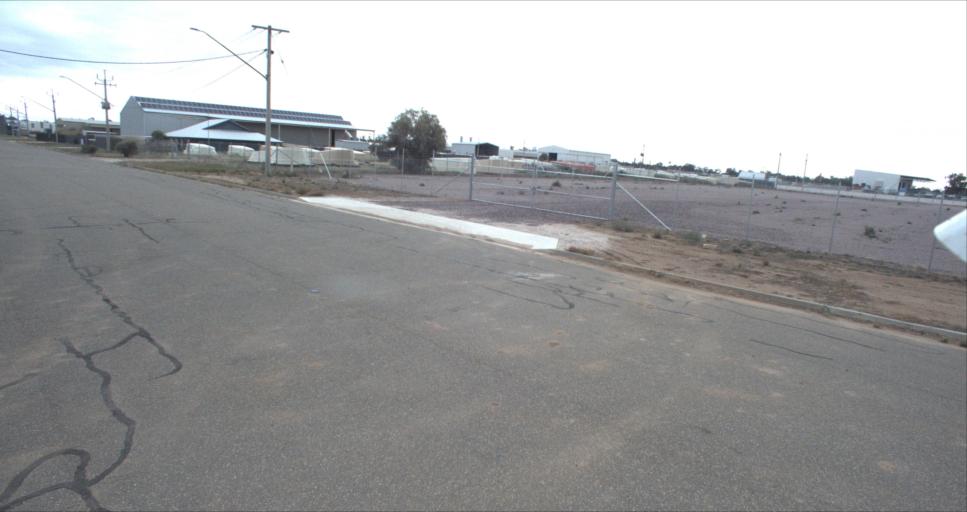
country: AU
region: New South Wales
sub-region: Leeton
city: Leeton
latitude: -34.5437
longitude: 146.3900
